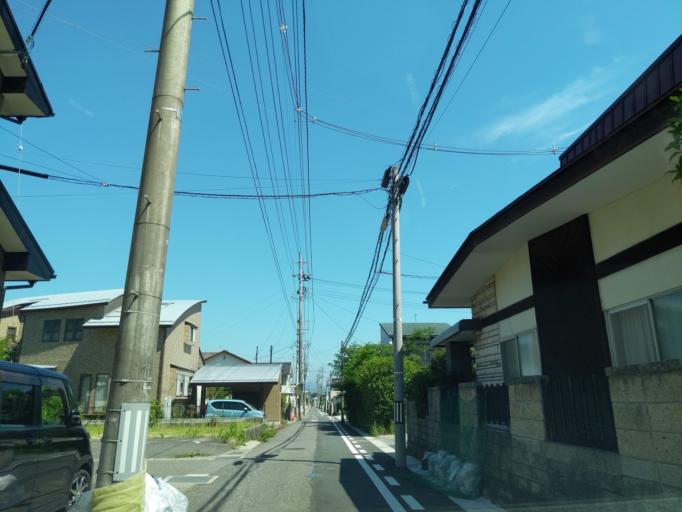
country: JP
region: Fukushima
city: Koriyama
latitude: 37.3887
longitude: 140.3576
